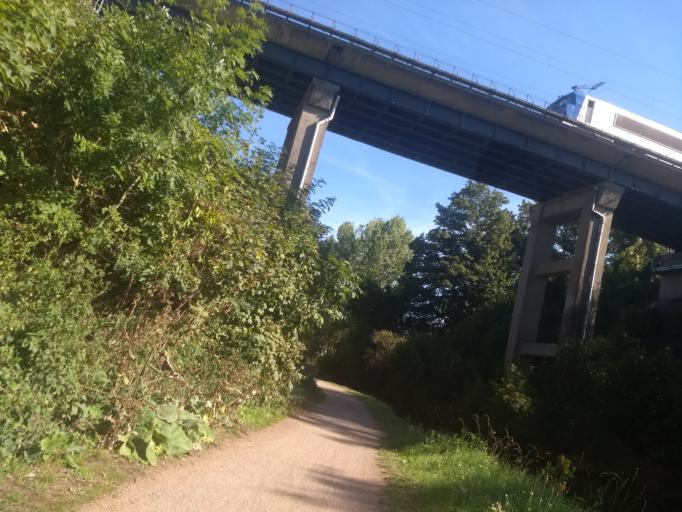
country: FR
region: Nord-Pas-de-Calais
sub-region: Departement du Pas-de-Calais
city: Saint-Laurent-Blangy
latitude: 50.3007
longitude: 2.8222
